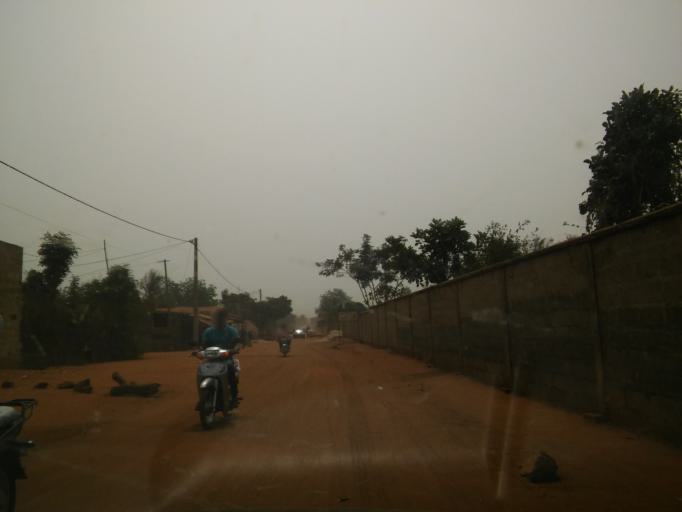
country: BJ
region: Mono
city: Come
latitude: 6.4088
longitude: 1.8784
